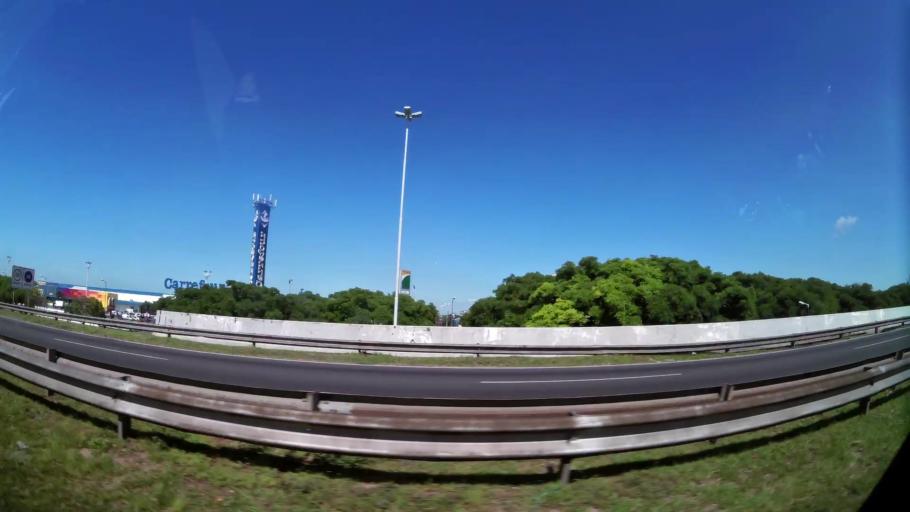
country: AR
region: Buenos Aires
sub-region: Partido de Tigre
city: Tigre
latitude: -34.4529
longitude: -58.5749
